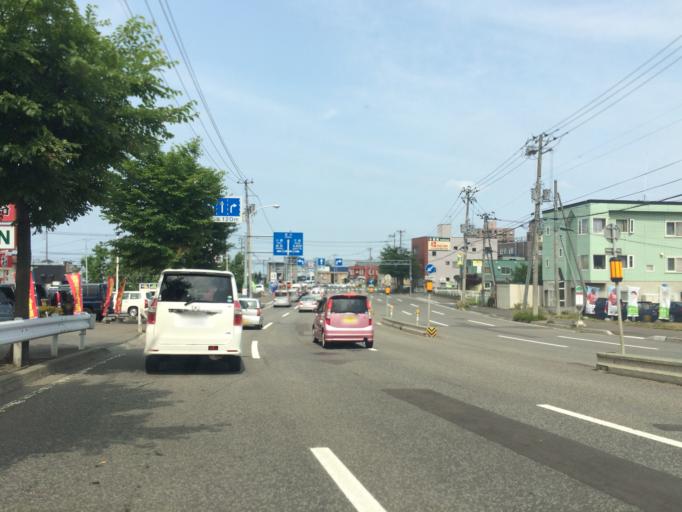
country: JP
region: Hokkaido
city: Sapporo
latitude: 43.0939
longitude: 141.2608
